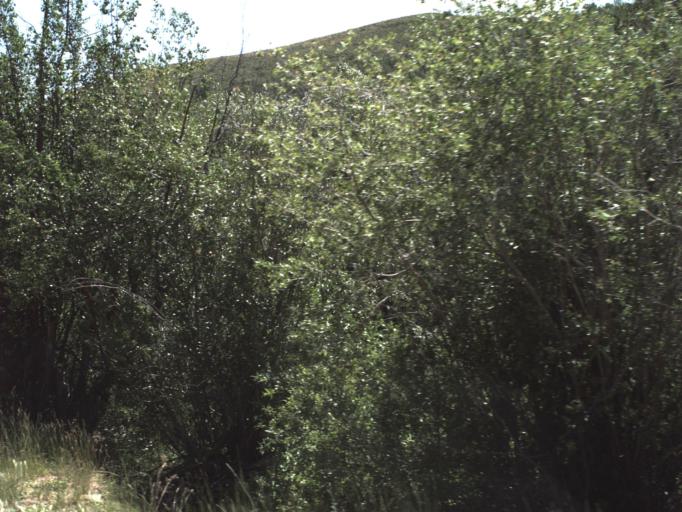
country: US
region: Utah
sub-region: Weber County
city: Wolf Creek
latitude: 41.3830
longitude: -111.5930
